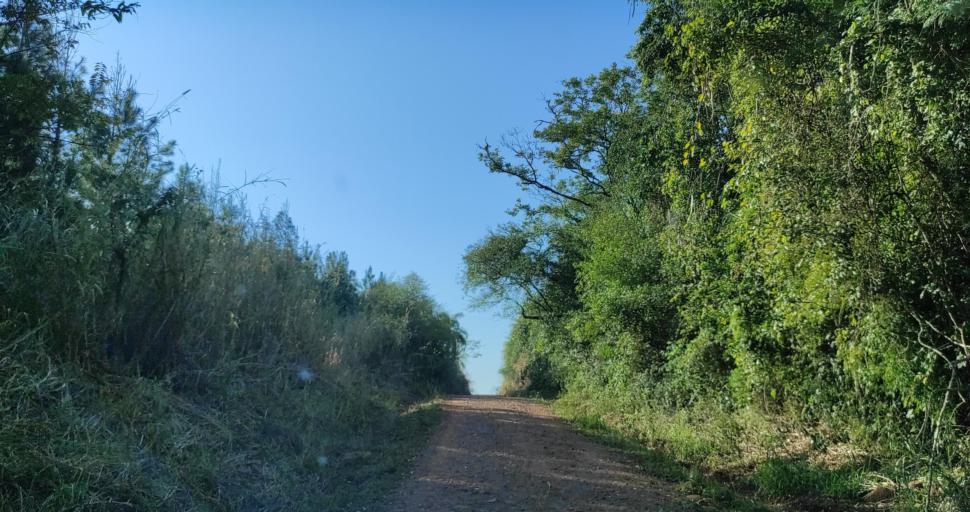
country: AR
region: Misiones
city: Capiovi
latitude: -26.8831
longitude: -55.1076
